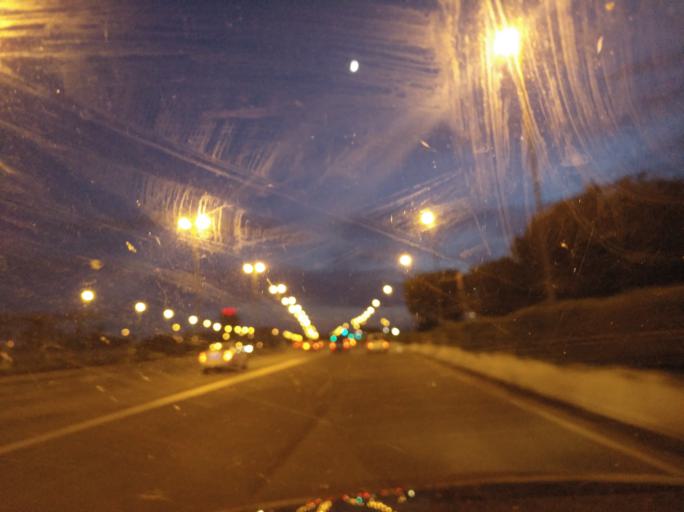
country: ES
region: Andalusia
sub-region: Provincia de Sevilla
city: Camas
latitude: 37.3934
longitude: -6.0134
